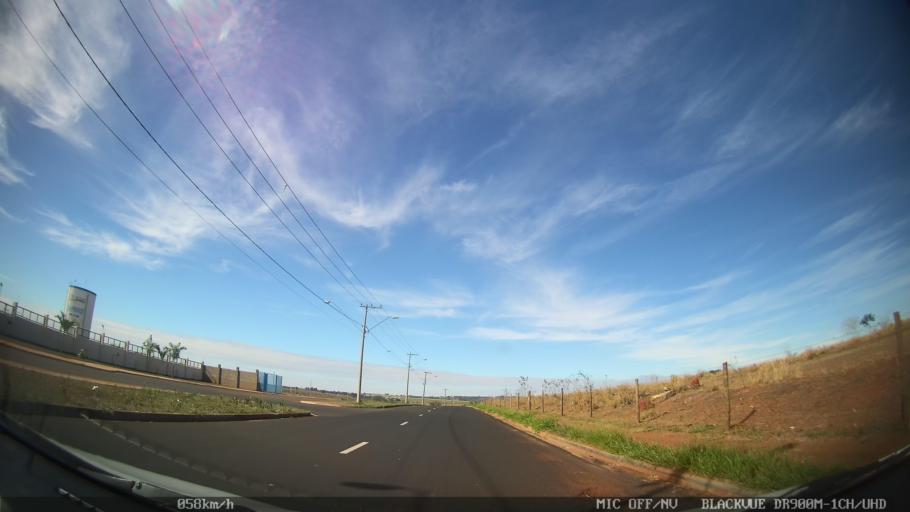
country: BR
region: Sao Paulo
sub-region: Sao Jose Do Rio Preto
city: Sao Jose do Rio Preto
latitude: -20.8044
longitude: -49.3204
